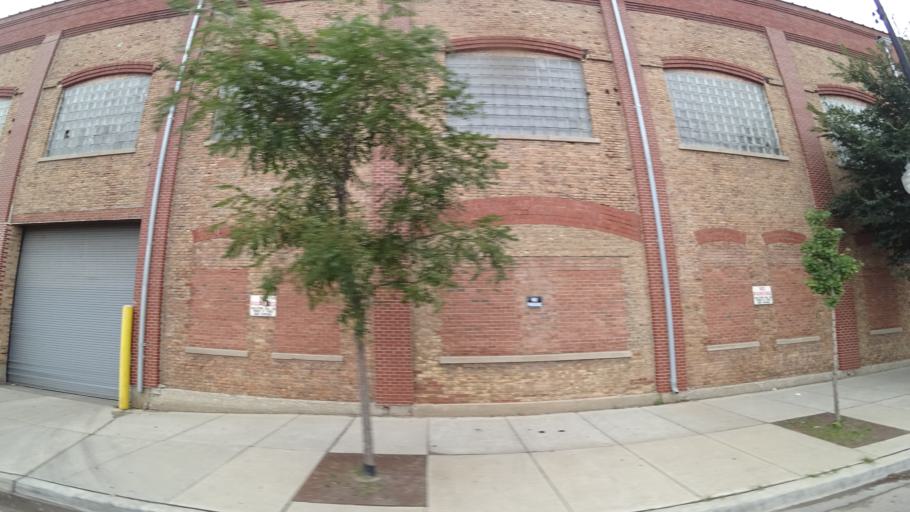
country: US
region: Illinois
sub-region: Cook County
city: Chicago
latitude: 41.8468
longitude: -87.6660
